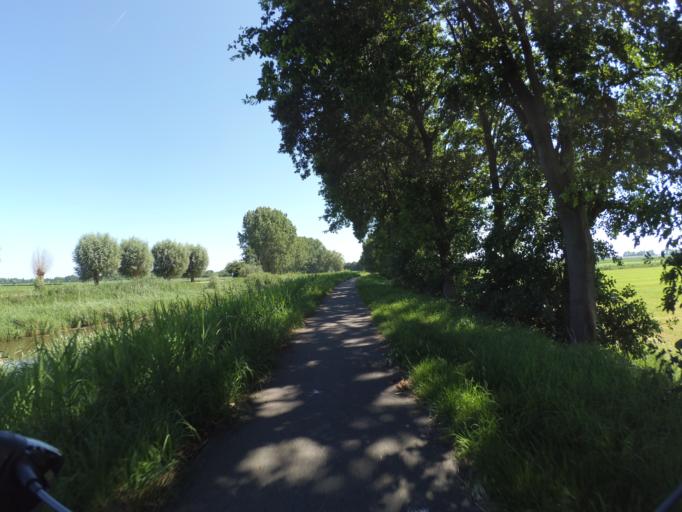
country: NL
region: North Brabant
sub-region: Gemeente Dongen
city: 's Gravenmoer
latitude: 51.6660
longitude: 4.9305
